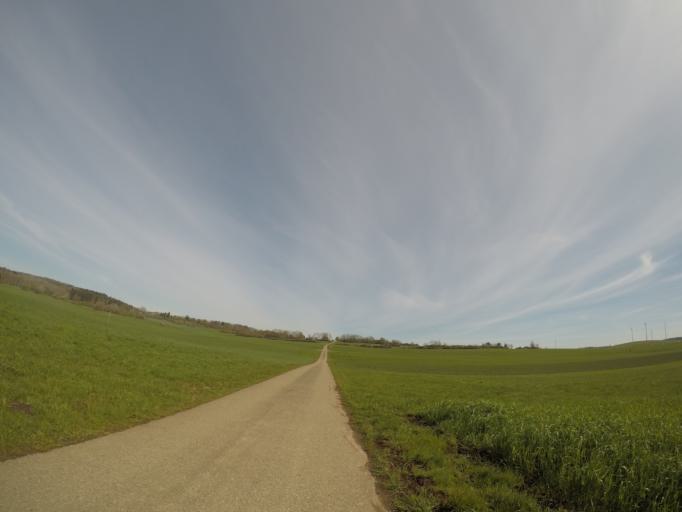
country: DE
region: Baden-Wuerttemberg
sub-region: Regierungsbezirk Stuttgart
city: Hohenstadt
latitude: 48.5249
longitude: 9.6700
